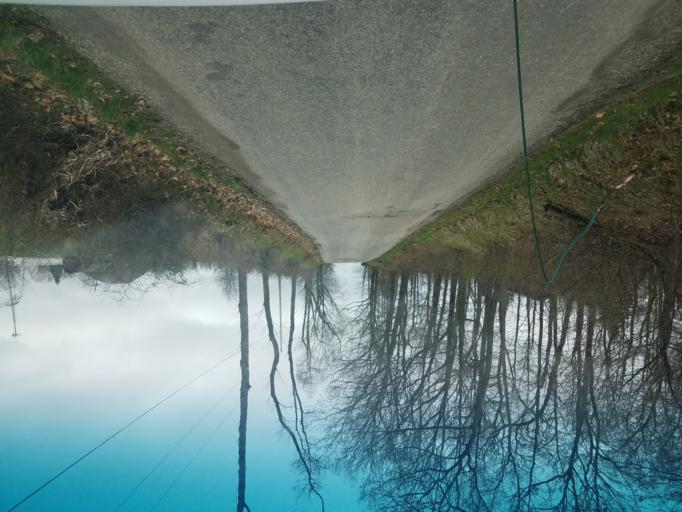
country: US
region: Ohio
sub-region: Stark County
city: Beach City
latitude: 40.6221
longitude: -81.6799
